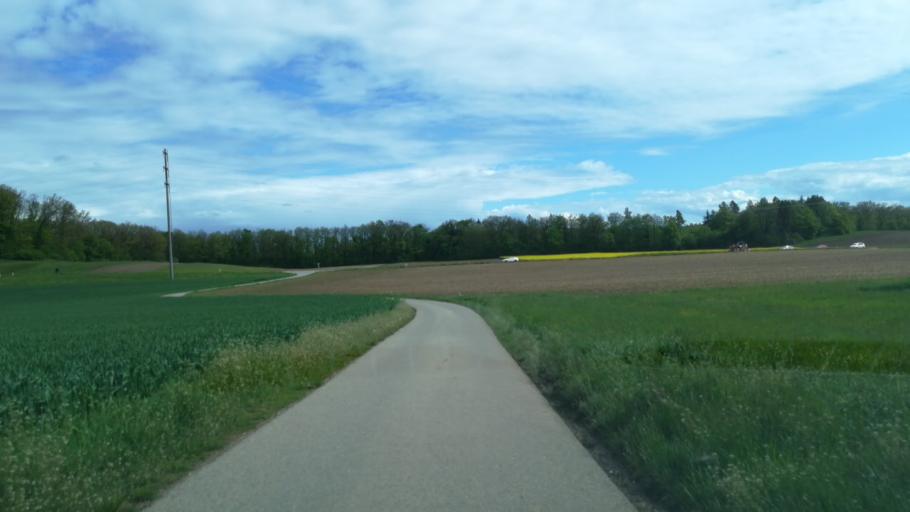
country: CH
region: Schaffhausen
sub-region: Bezirk Reiat
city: Stetten
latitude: 47.7407
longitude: 8.6769
